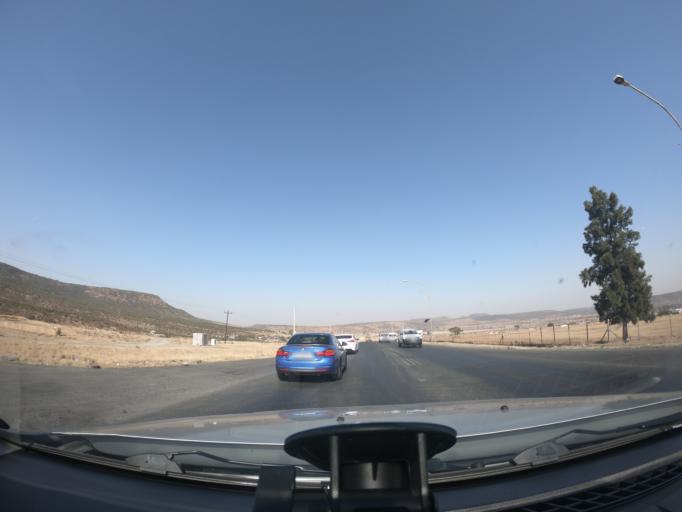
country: ZA
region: KwaZulu-Natal
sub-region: uThukela District Municipality
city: Ladysmith
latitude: -28.5721
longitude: 29.8341
